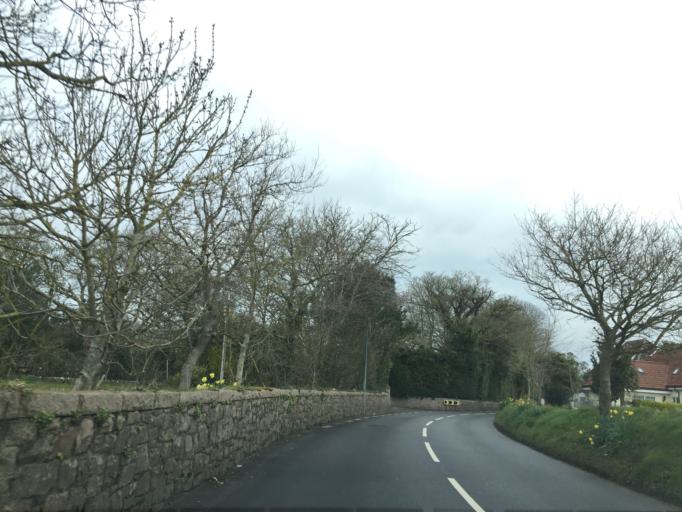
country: JE
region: St Helier
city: Saint Helier
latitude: 49.2119
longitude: -2.1418
